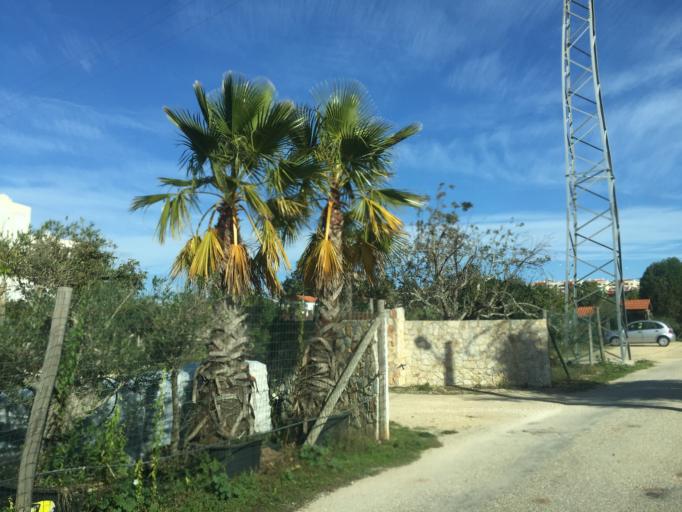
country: PT
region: Coimbra
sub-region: Figueira da Foz
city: Tavarede
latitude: 40.1652
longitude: -8.8432
